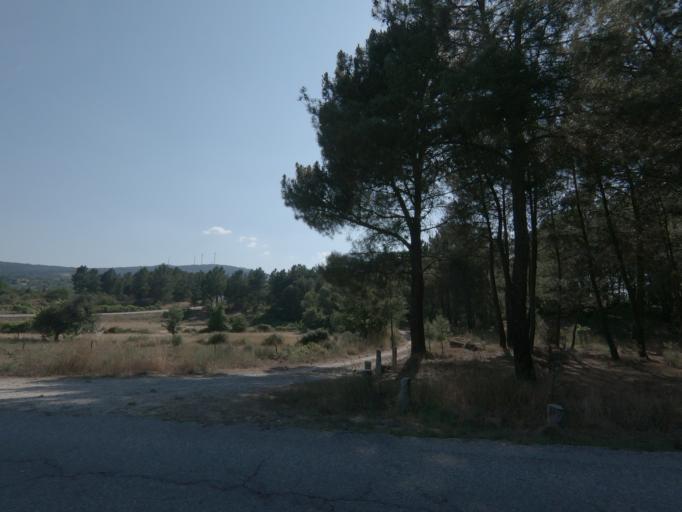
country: PT
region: Viseu
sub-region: Moimenta da Beira
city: Moimenta da Beira
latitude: 40.9751
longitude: -7.5772
